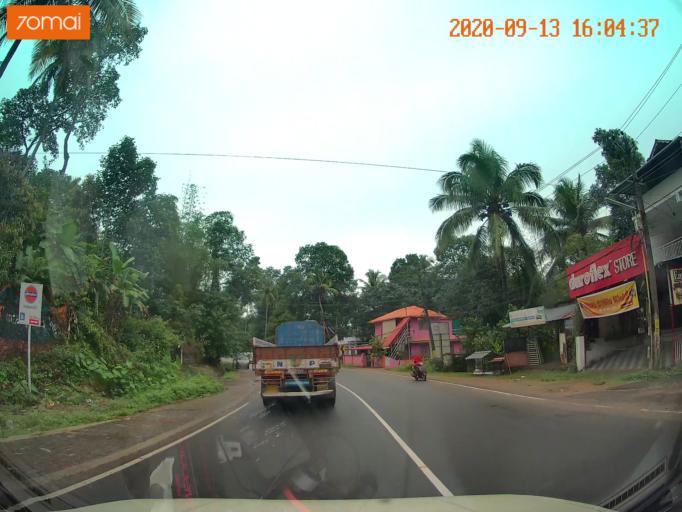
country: IN
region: Kerala
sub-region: Kottayam
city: Palackattumala
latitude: 9.6710
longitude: 76.5711
